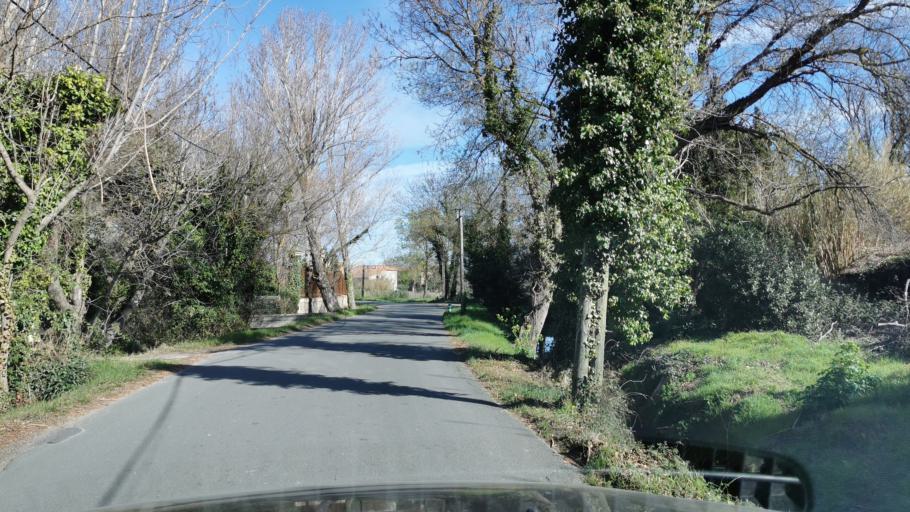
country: FR
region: Languedoc-Roussillon
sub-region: Departement de l'Aude
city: Narbonne
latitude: 43.1908
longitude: 2.9909
